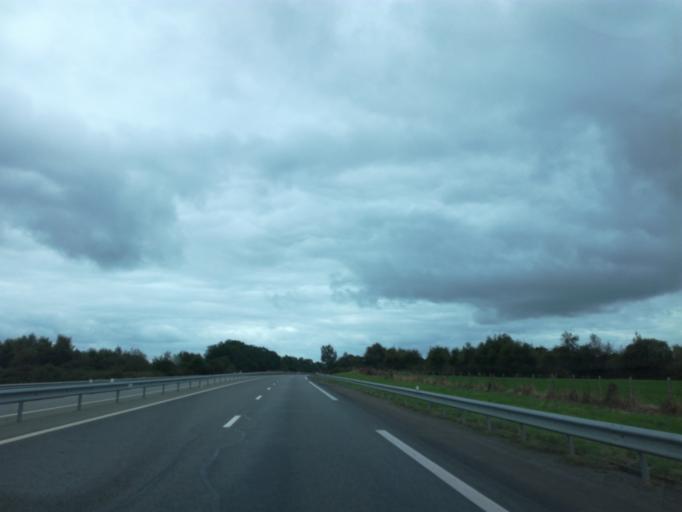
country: FR
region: Brittany
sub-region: Departement des Cotes-d'Armor
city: Plumaugat
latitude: 48.1914
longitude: -2.3042
